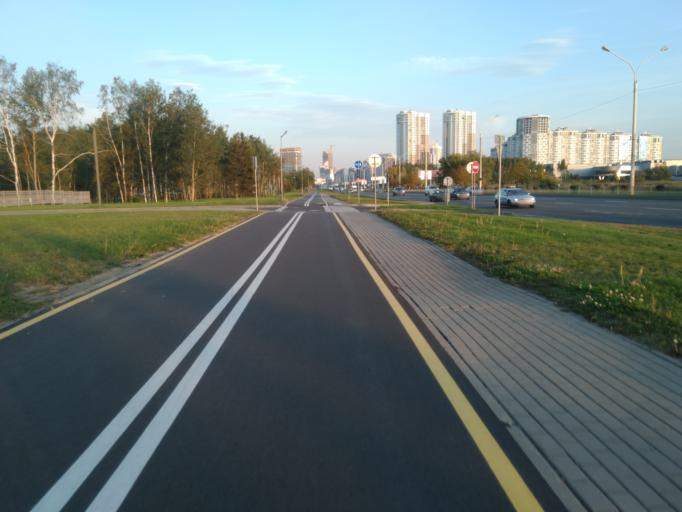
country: BY
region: Minsk
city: Zhdanovichy
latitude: 53.9478
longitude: 27.4544
